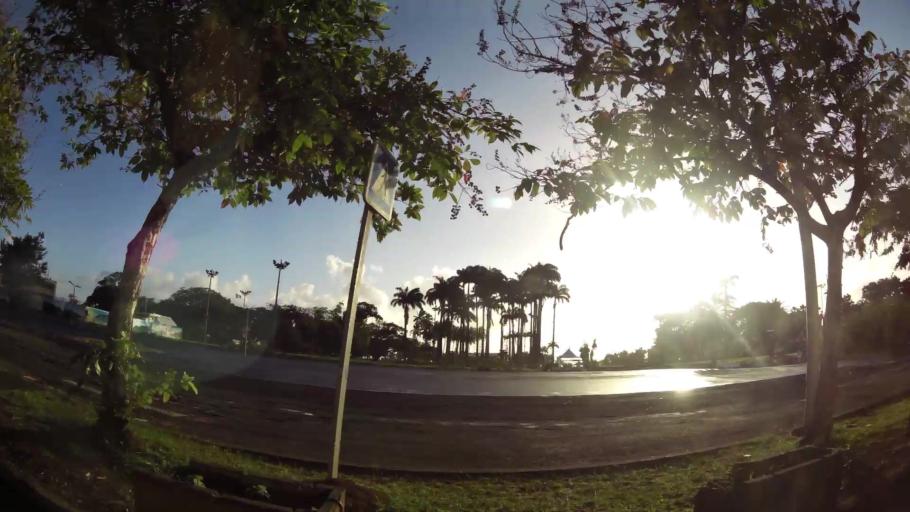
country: MQ
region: Martinique
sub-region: Martinique
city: Fort-de-France
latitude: 14.6042
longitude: -61.0667
